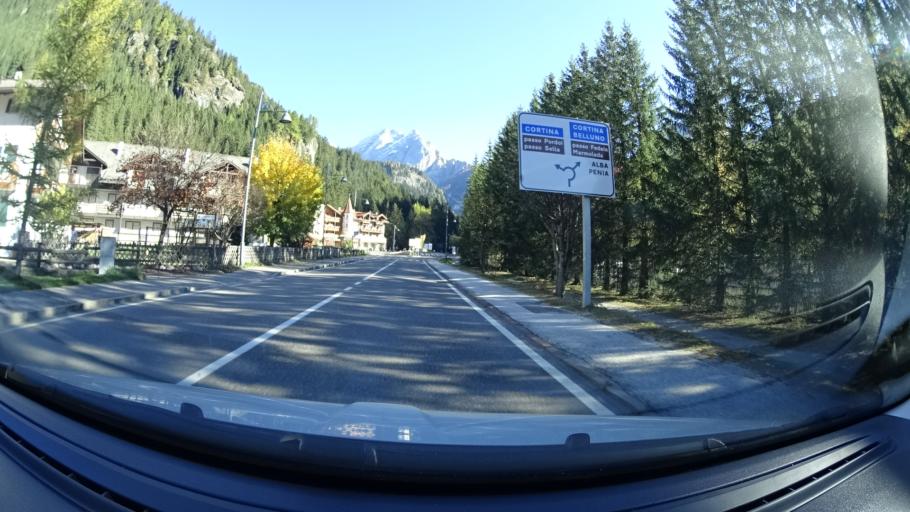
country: IT
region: Trentino-Alto Adige
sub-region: Provincia di Trento
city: Canazei
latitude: 46.4732
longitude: 11.7759
